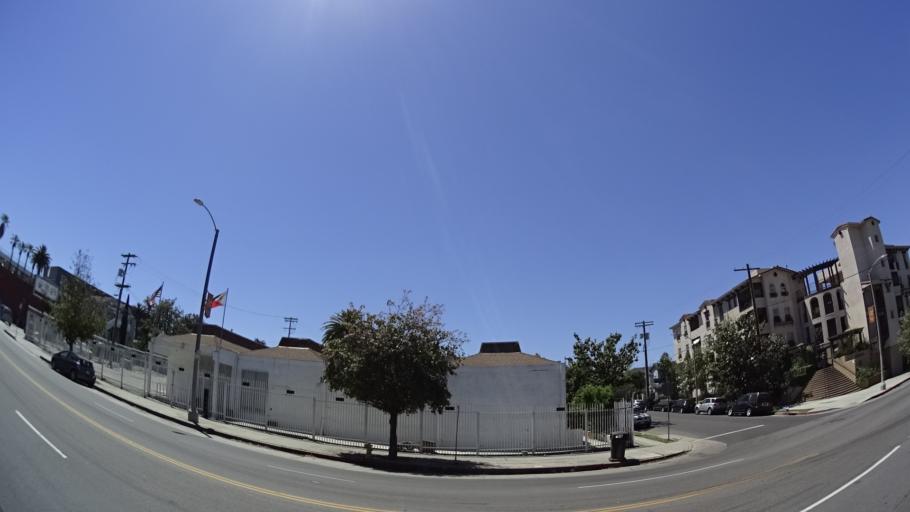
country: US
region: California
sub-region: Los Angeles County
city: Echo Park
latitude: 34.0690
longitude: -118.2639
